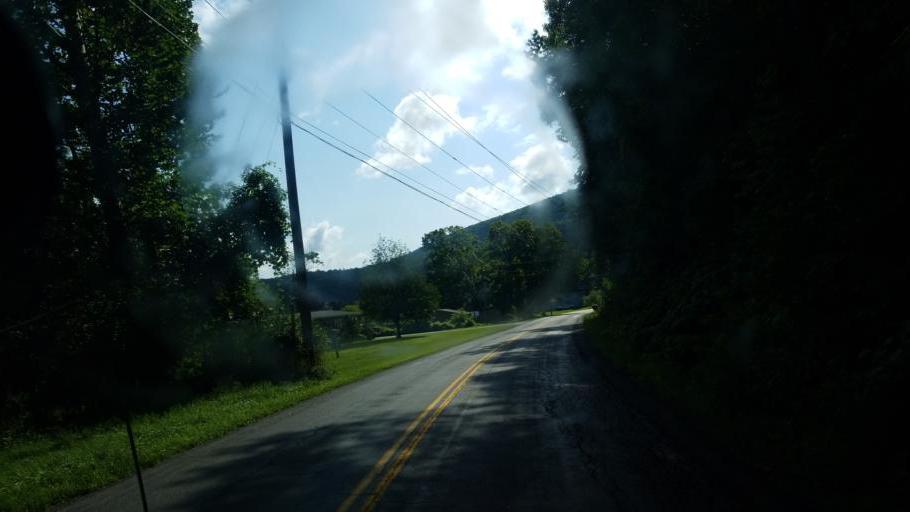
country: US
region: New York
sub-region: Steuben County
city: Canisteo
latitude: 42.2610
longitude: -77.6170
